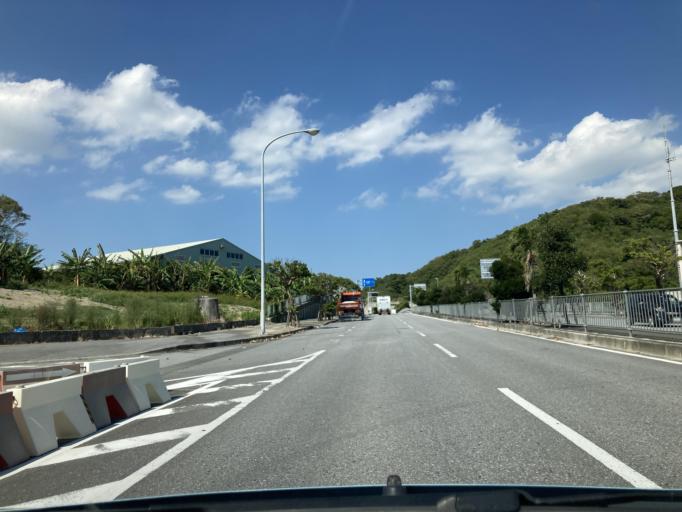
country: JP
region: Okinawa
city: Tomigusuku
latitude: 26.1845
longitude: 127.7218
